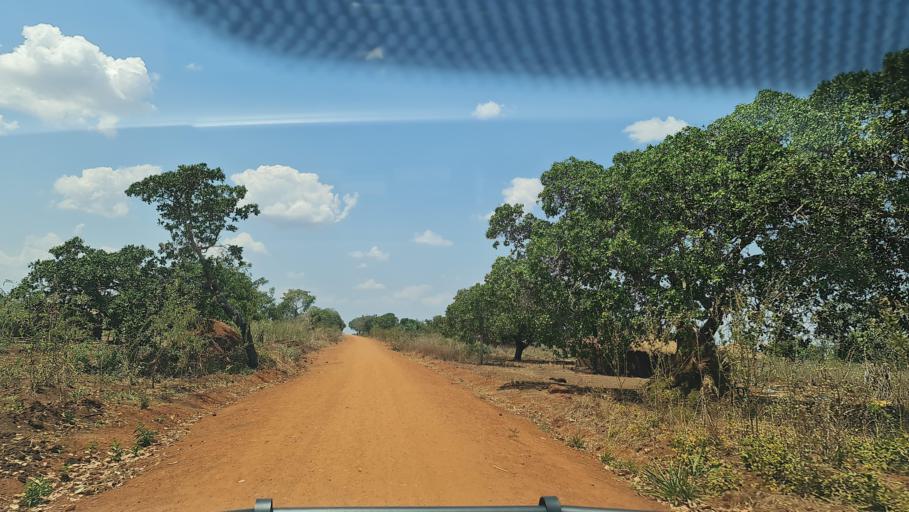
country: MZ
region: Nampula
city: Nacala
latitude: -14.7940
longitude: 40.0675
